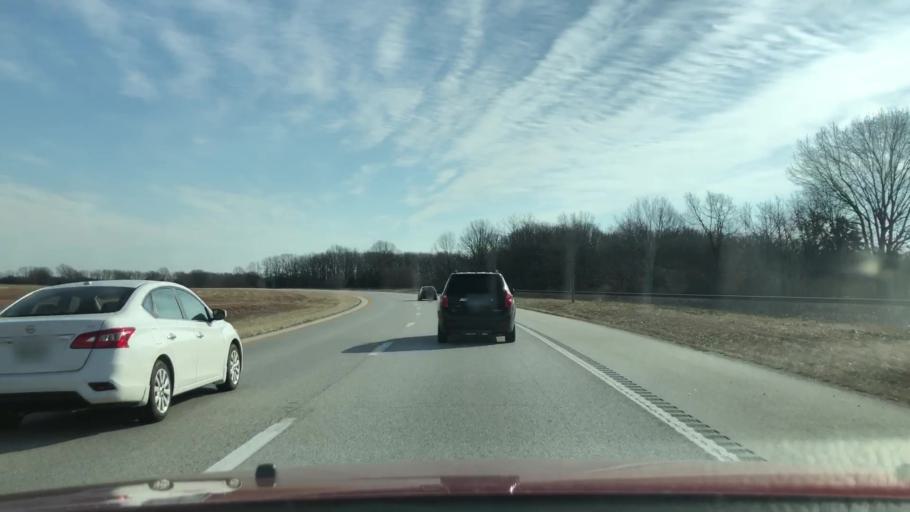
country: US
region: Missouri
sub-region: Webster County
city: Seymour
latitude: 37.1303
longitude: -92.7383
